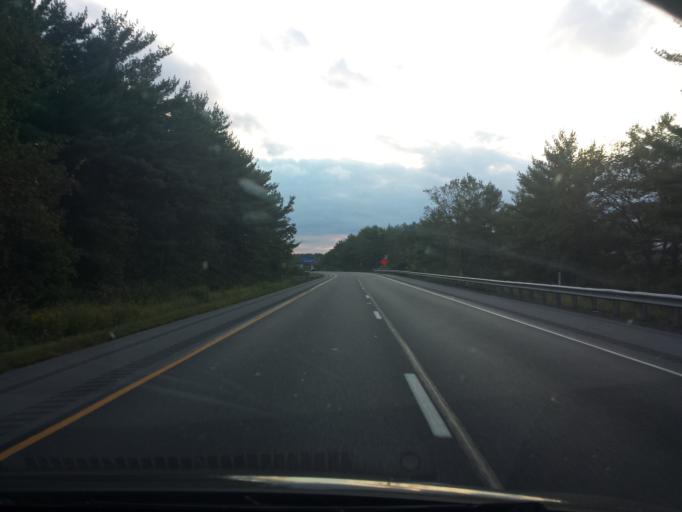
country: US
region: Pennsylvania
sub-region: Montour County
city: Danville
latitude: 40.9994
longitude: -76.6357
